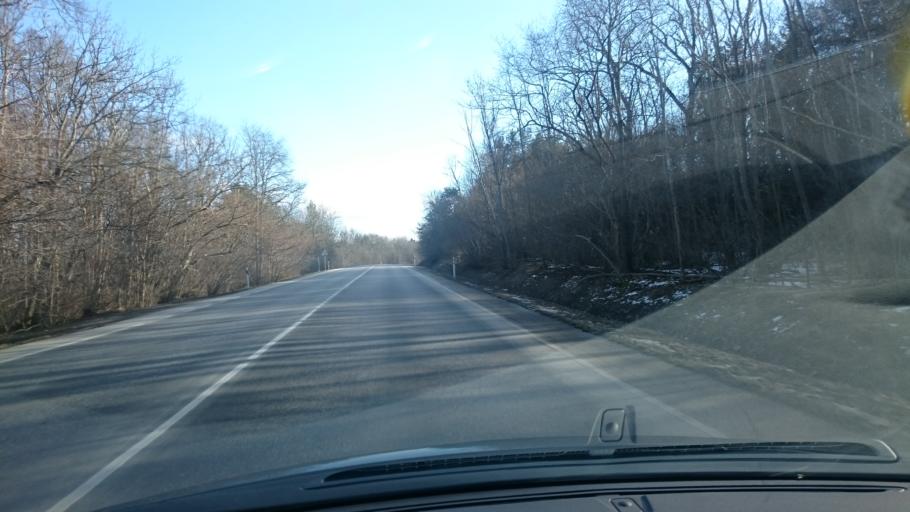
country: EE
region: Harju
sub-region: Keila linn
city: Keila
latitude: 59.4209
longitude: 24.3340
